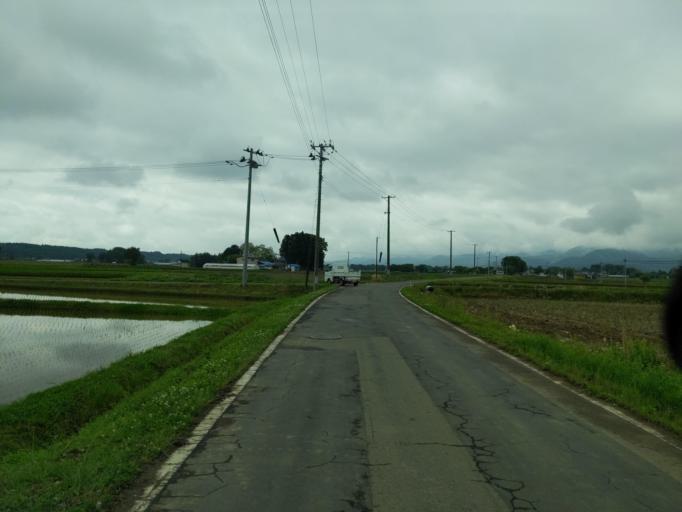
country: JP
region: Fukushima
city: Koriyama
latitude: 37.3536
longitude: 140.3065
